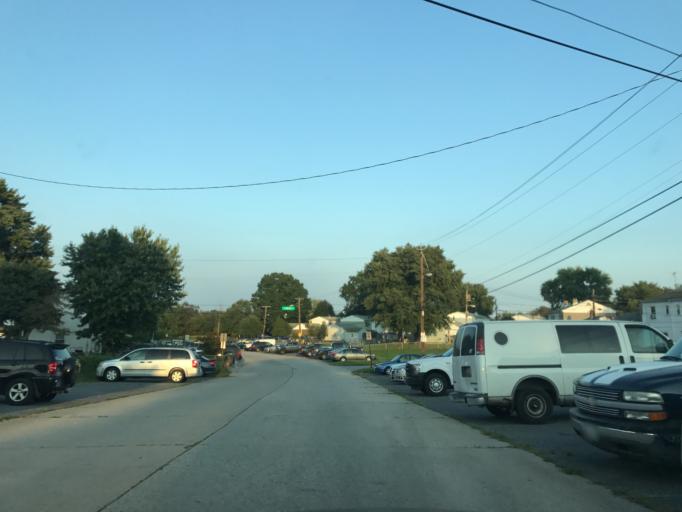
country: US
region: Maryland
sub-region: Baltimore County
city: Rosedale
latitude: 39.3054
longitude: -76.5479
